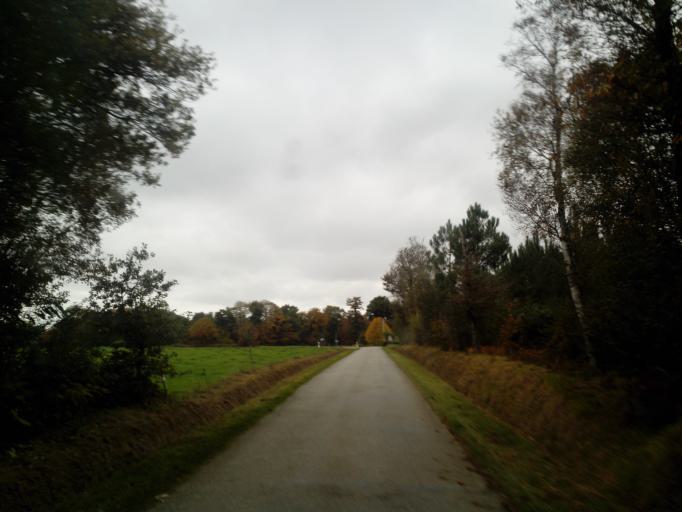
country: FR
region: Brittany
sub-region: Departement du Morbihan
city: Meneac
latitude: 48.1204
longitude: -2.4050
